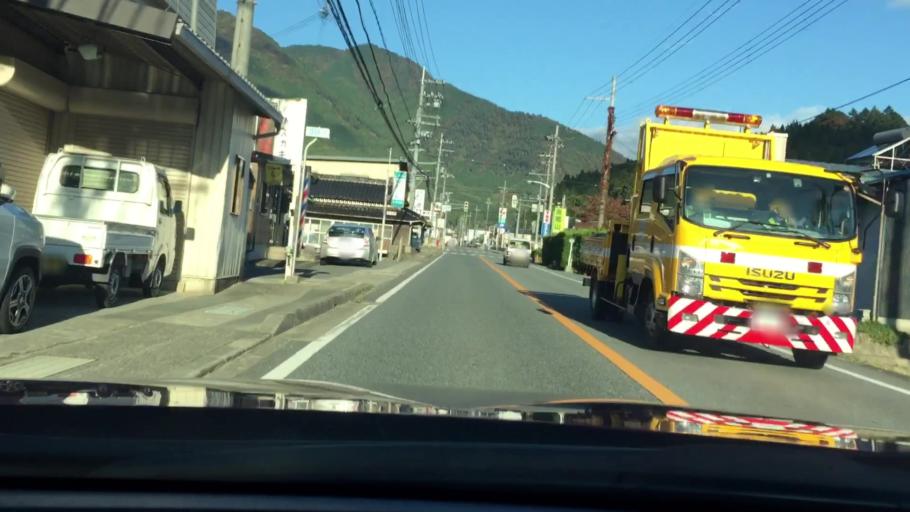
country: JP
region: Hyogo
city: Yamazakicho-nakabirose
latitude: 35.1092
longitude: 134.5783
